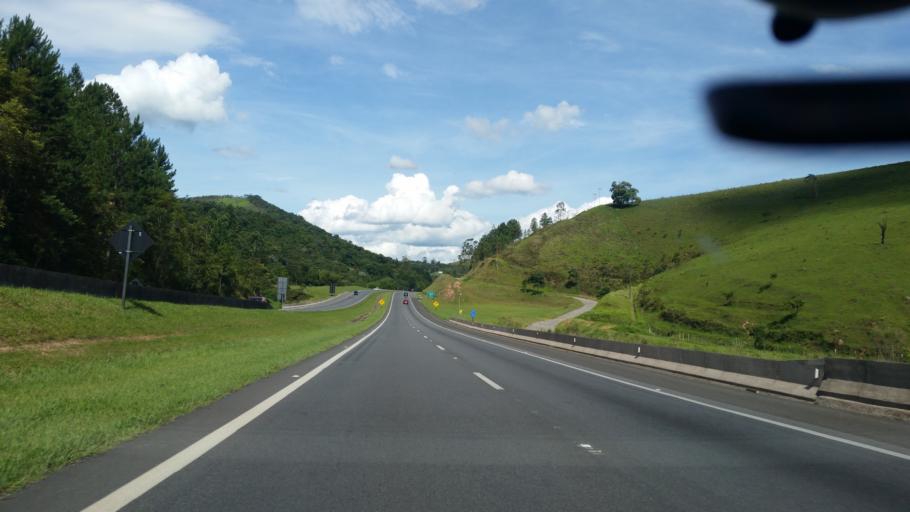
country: BR
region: Sao Paulo
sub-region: Piracaia
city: Piracaia
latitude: -23.1731
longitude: -46.2758
